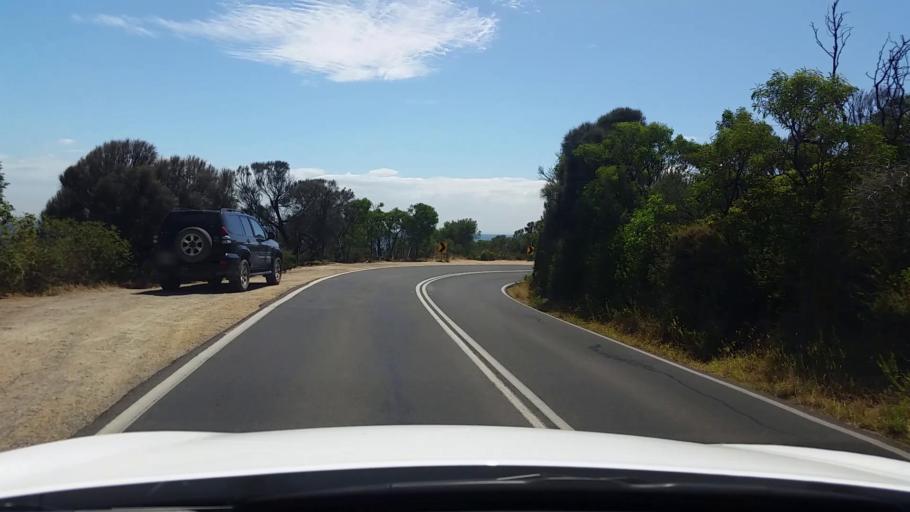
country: AU
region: Victoria
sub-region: Mornington Peninsula
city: Mount Martha
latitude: -38.2718
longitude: 145.0018
